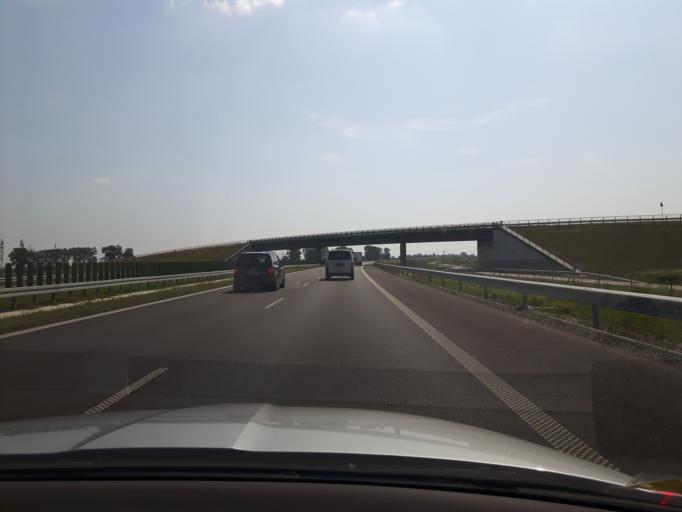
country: PL
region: Pomeranian Voivodeship
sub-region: Powiat nowodworski
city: Nowy Dwor Gdanski
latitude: 54.1882
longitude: 19.1675
